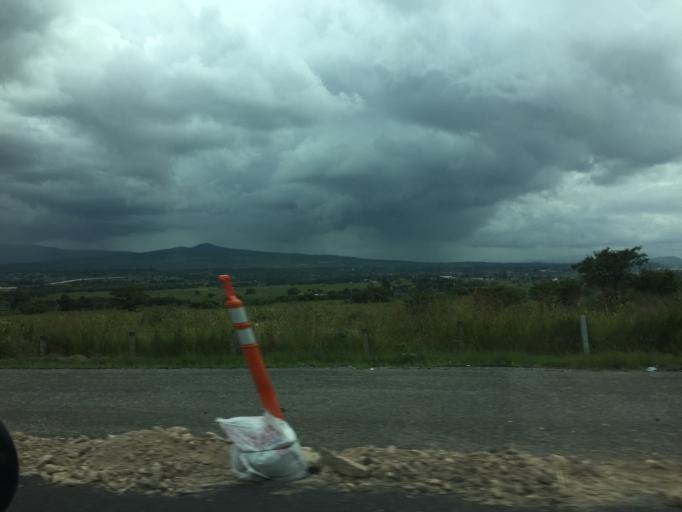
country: MX
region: Jalisco
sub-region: Zapotlanejo
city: La Mezquitera
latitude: 20.5893
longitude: -103.1028
